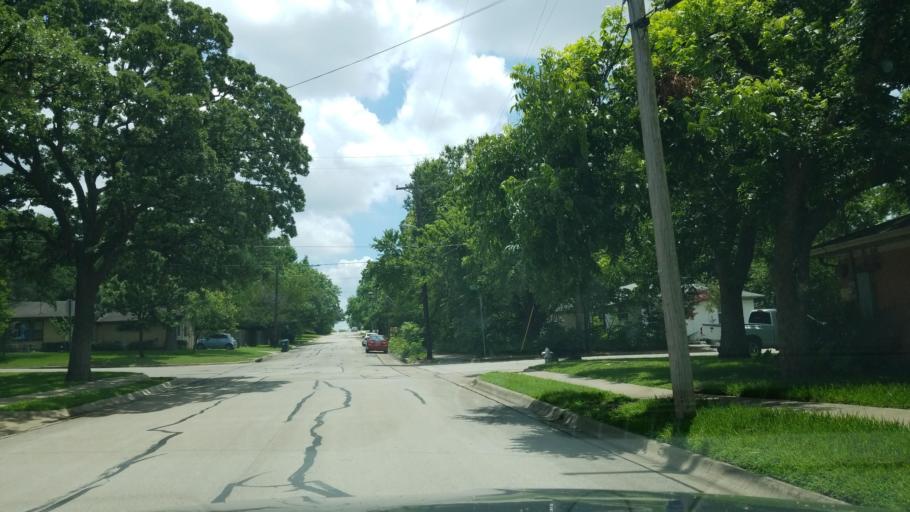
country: US
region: Texas
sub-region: Denton County
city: Denton
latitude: 33.2366
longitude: -97.1164
